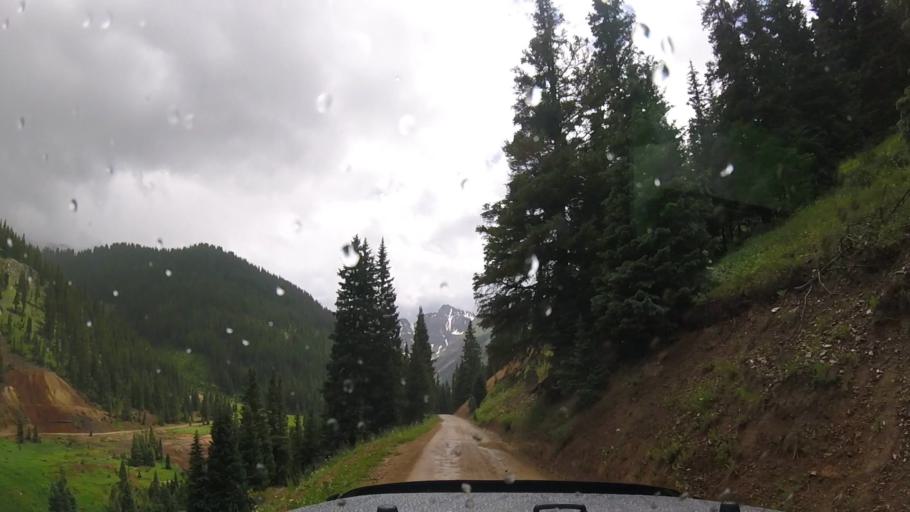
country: US
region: Colorado
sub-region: San Juan County
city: Silverton
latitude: 37.8989
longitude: -107.6470
